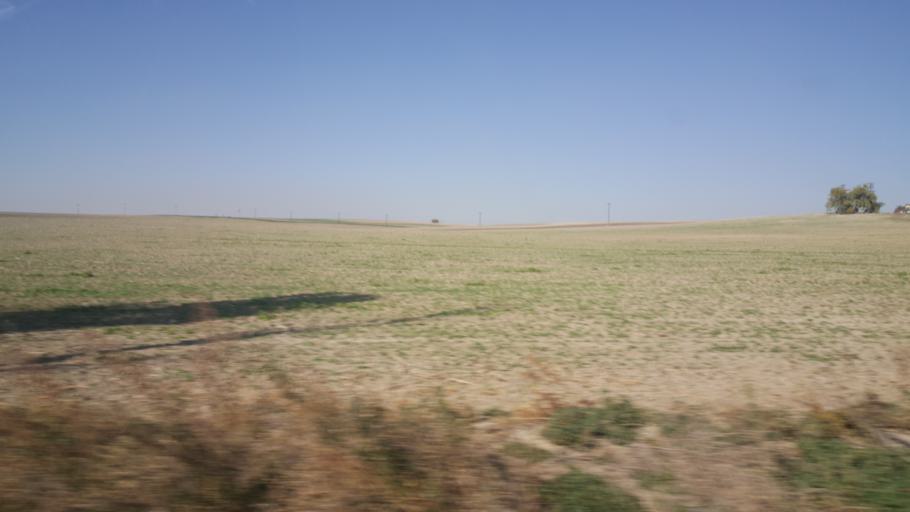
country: TR
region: Konya
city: Celtik
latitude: 39.0644
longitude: 31.8883
